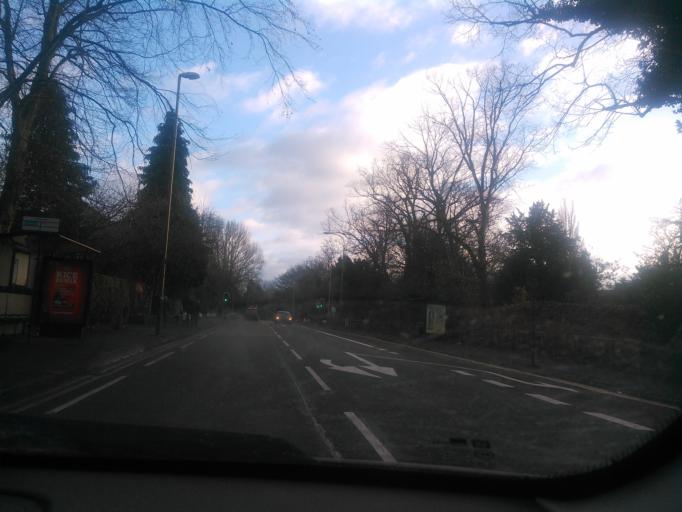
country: GB
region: England
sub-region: Leicestershire
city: Oadby
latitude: 52.6130
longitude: -1.1026
